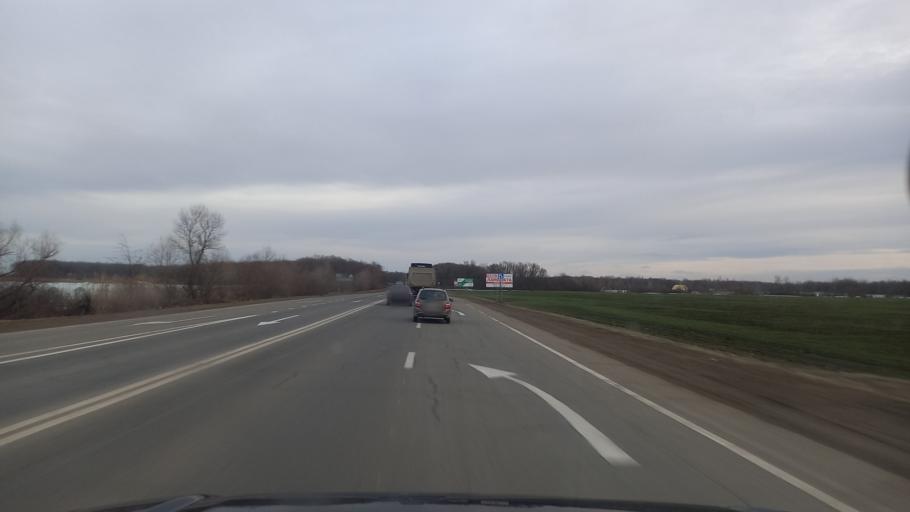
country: RU
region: Krasnodarskiy
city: Yuzhnyy
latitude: 44.7418
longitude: 39.9329
